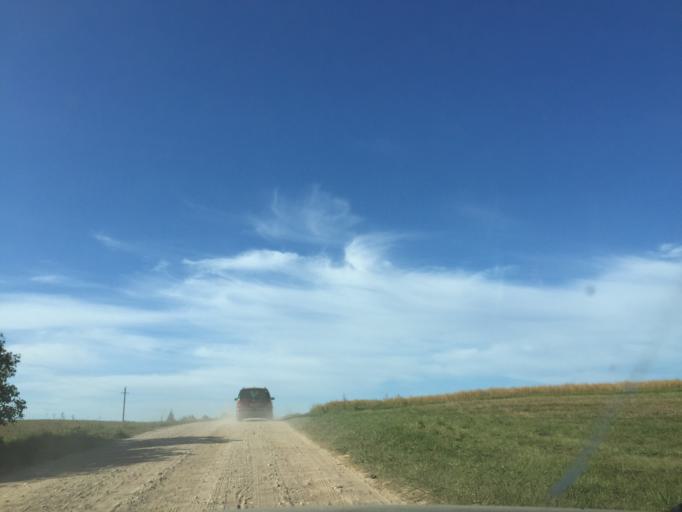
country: LT
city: Zarasai
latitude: 55.7955
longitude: 25.9519
